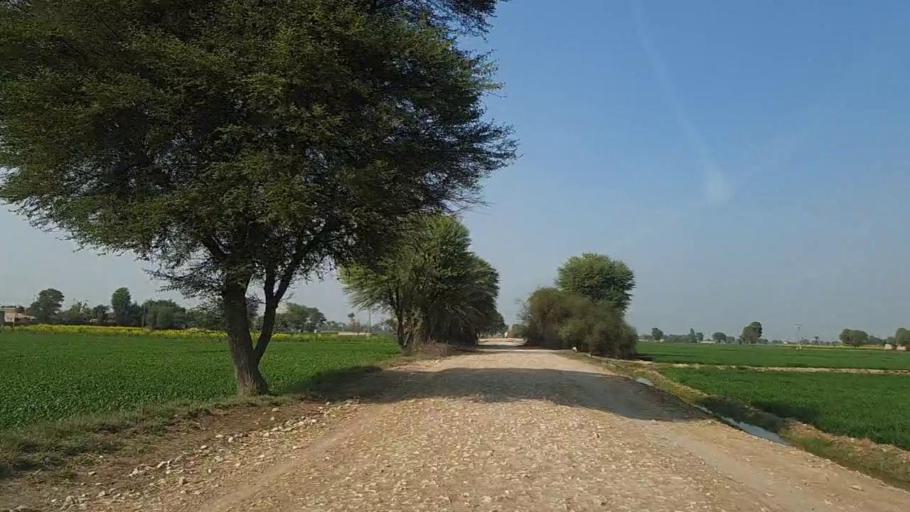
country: PK
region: Sindh
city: Moro
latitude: 26.6981
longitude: 67.9518
